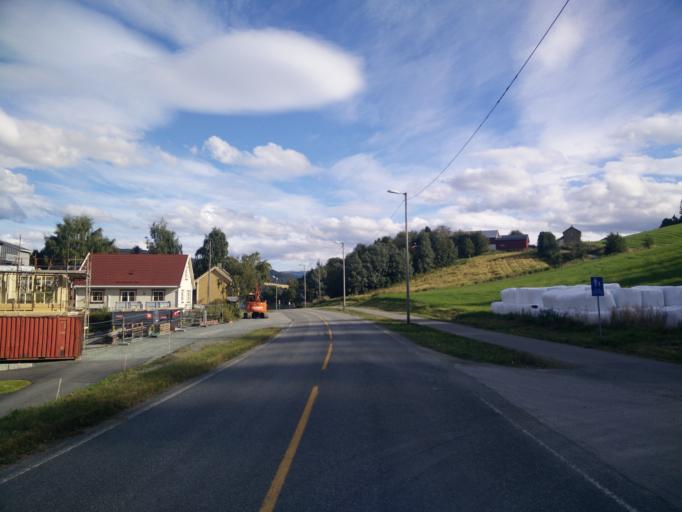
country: NO
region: Sor-Trondelag
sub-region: Skaun
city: Borsa
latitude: 63.3191
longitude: 10.1446
